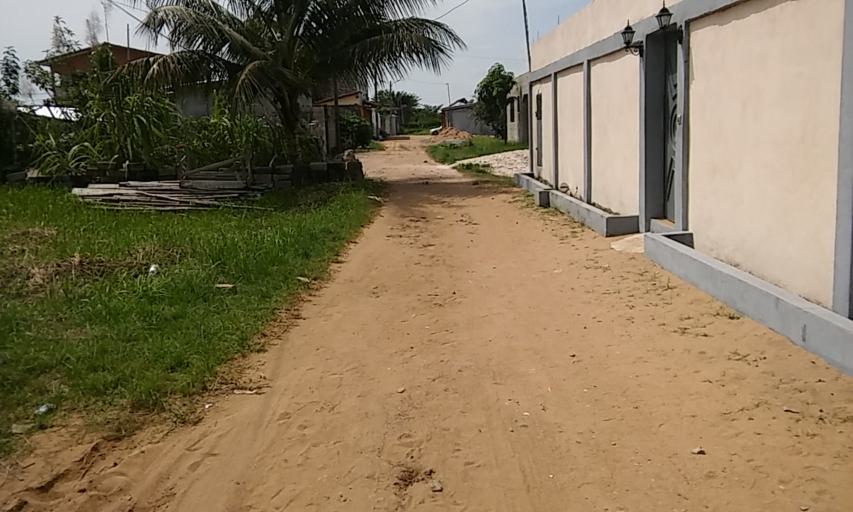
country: CI
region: Sud-Comoe
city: Grand-Bassam
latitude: 5.2183
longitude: -3.7449
